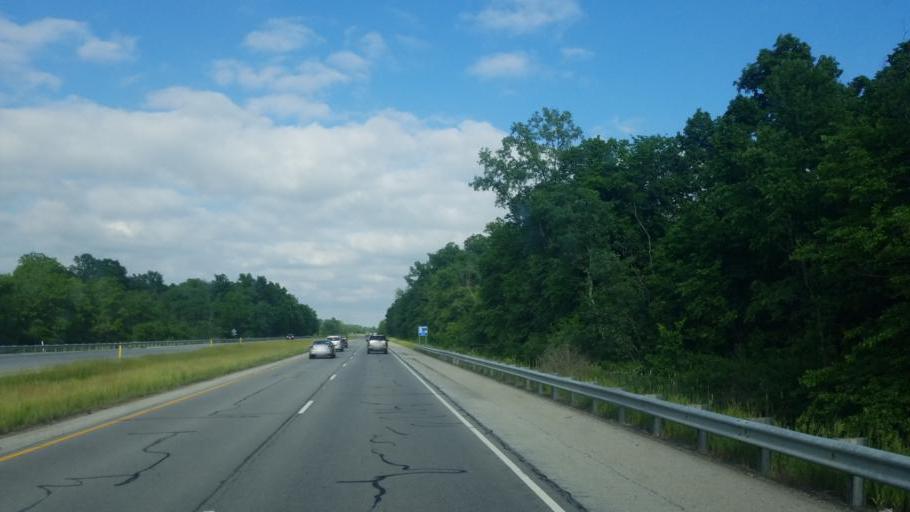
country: US
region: Indiana
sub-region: Whitley County
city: Churubusco
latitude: 41.1250
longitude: -85.2644
